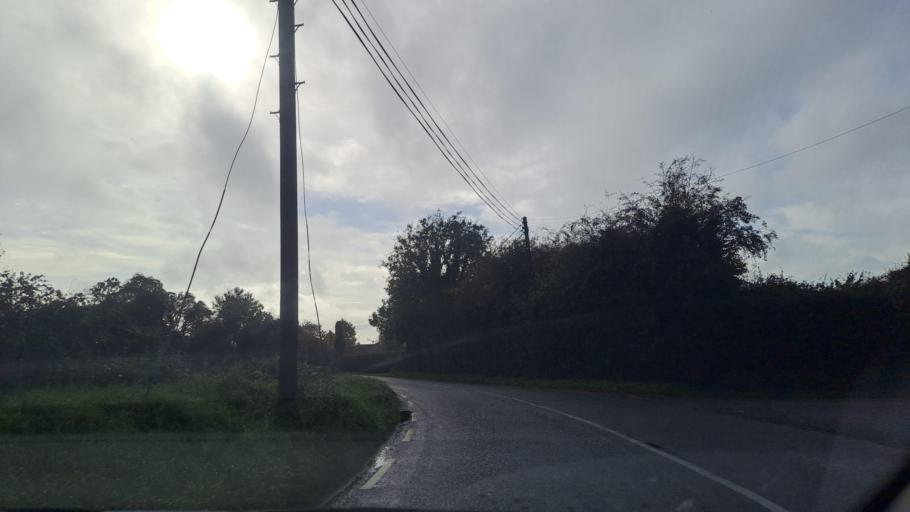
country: IE
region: Ulster
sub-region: County Monaghan
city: Carrickmacross
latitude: 53.9417
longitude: -6.7168
